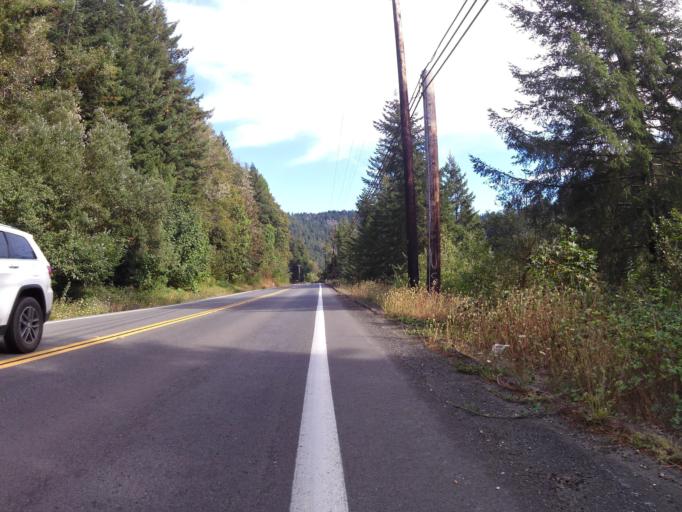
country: US
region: California
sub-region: Del Norte County
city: Bertsch-Oceanview
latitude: 41.8159
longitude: -124.0897
